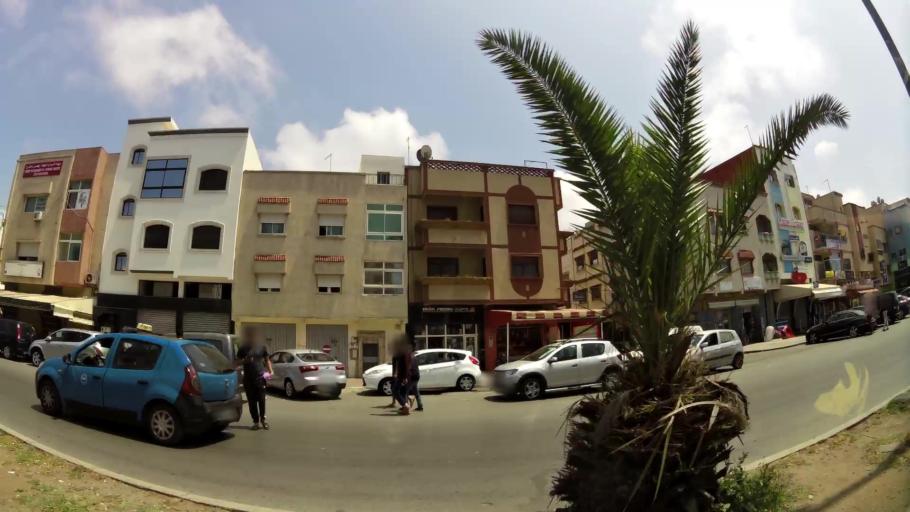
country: MA
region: Rabat-Sale-Zemmour-Zaer
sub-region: Skhirate-Temara
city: Temara
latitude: 33.9746
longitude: -6.8893
